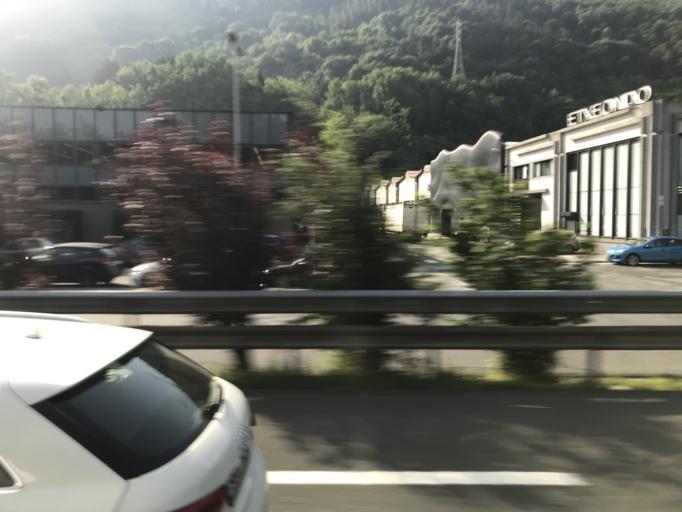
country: ES
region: Basque Country
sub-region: Provincia de Guipuzcoa
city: Irura
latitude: 43.1723
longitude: -2.0612
